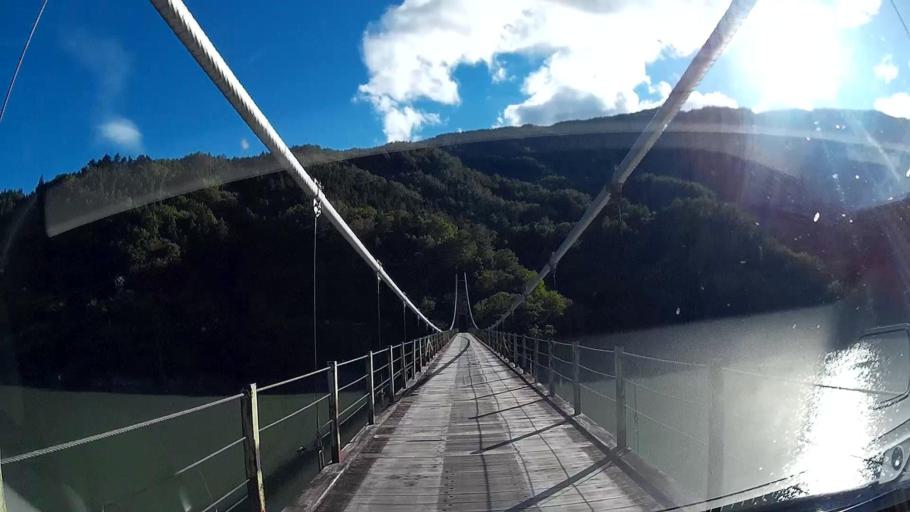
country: JP
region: Shizuoka
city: Shizuoka-shi
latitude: 35.2402
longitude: 138.2502
